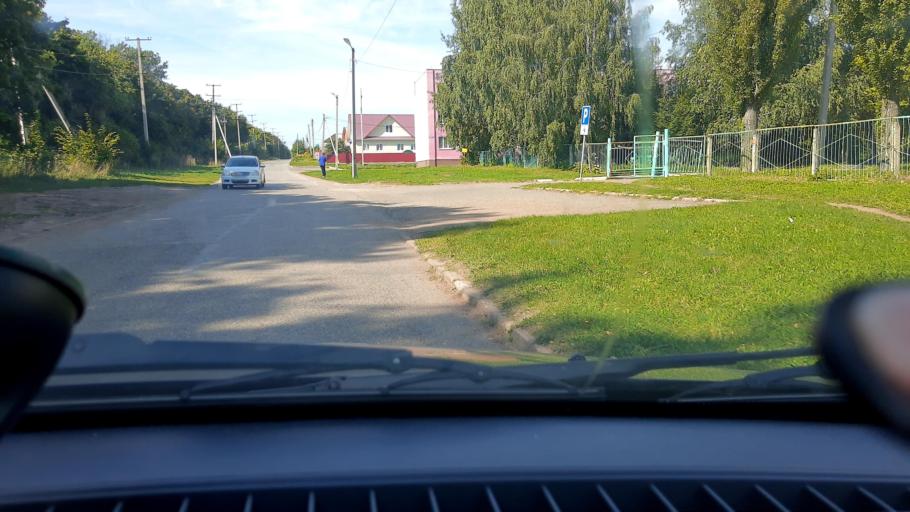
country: RU
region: Bashkortostan
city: Avdon
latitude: 54.6726
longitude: 55.7130
